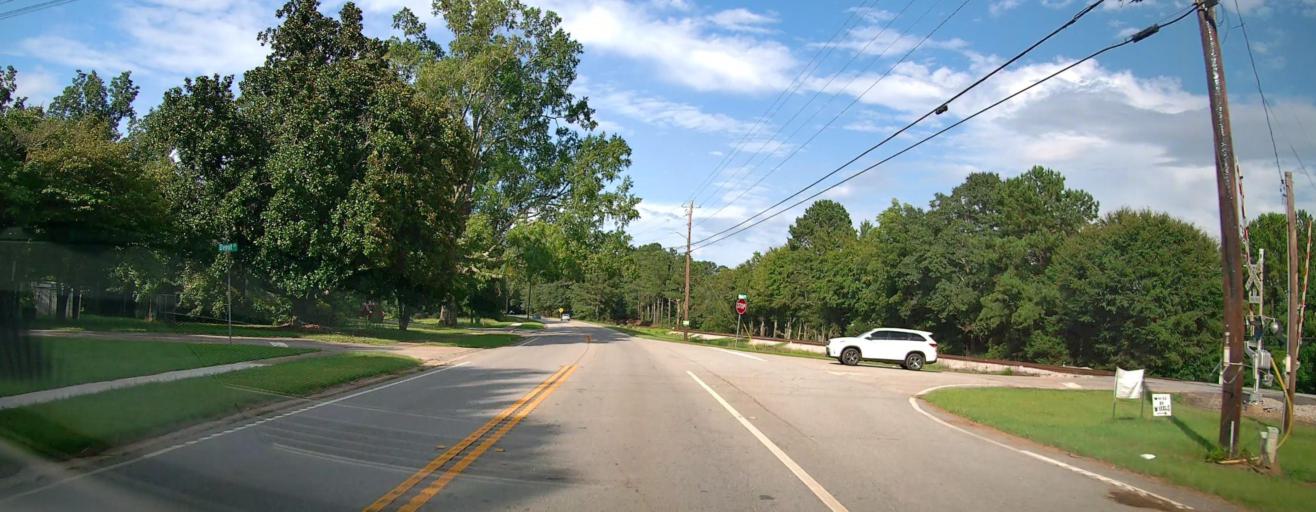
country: US
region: Georgia
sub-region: Coweta County
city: Senoia
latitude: 33.2272
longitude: -84.5700
